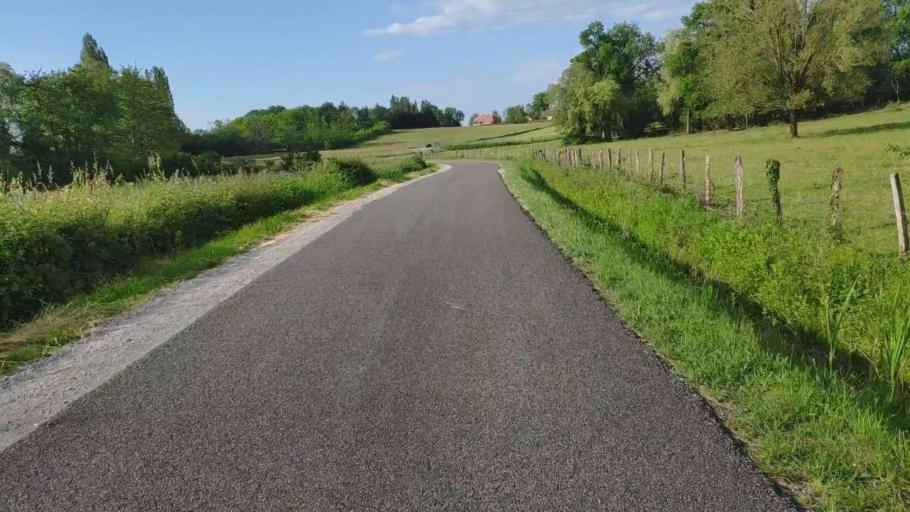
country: FR
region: Franche-Comte
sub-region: Departement du Jura
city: Bletterans
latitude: 46.7537
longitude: 5.4489
